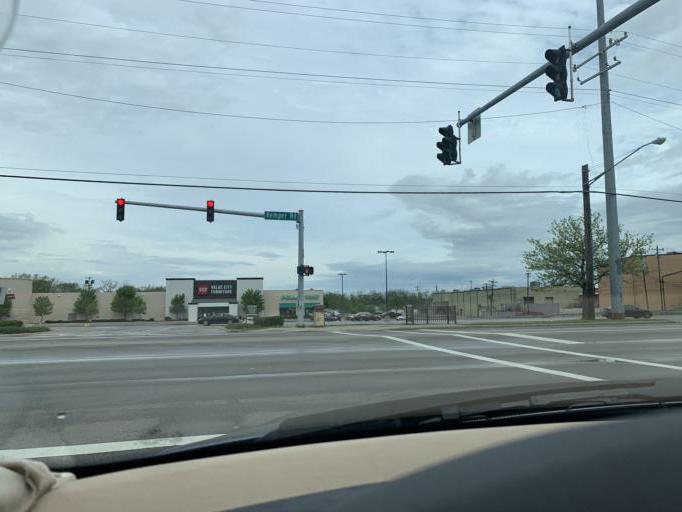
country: US
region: Ohio
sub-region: Hamilton County
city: Springdale
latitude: 39.2877
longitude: -84.4707
